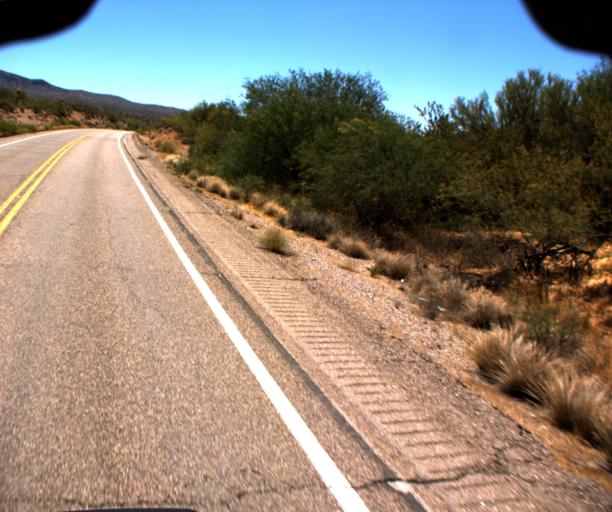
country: US
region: Arizona
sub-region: Pinal County
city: Kearny
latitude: 33.1169
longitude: -110.9641
